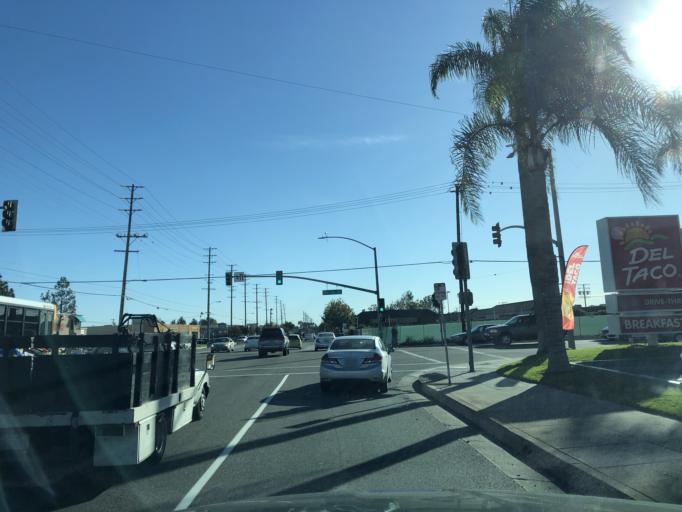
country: US
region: California
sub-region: Orange County
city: Tustin
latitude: 33.7675
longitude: -117.8359
